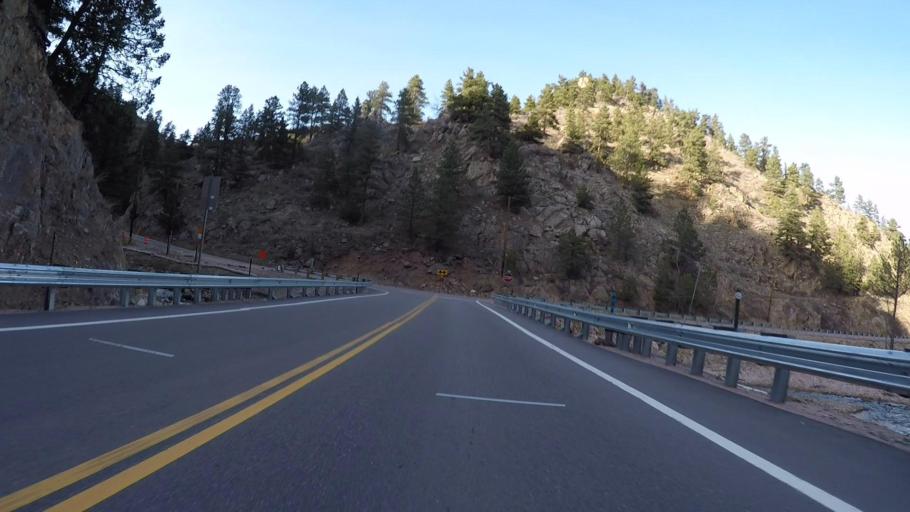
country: US
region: Colorado
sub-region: Boulder County
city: Boulder
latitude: 40.1017
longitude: -105.3423
